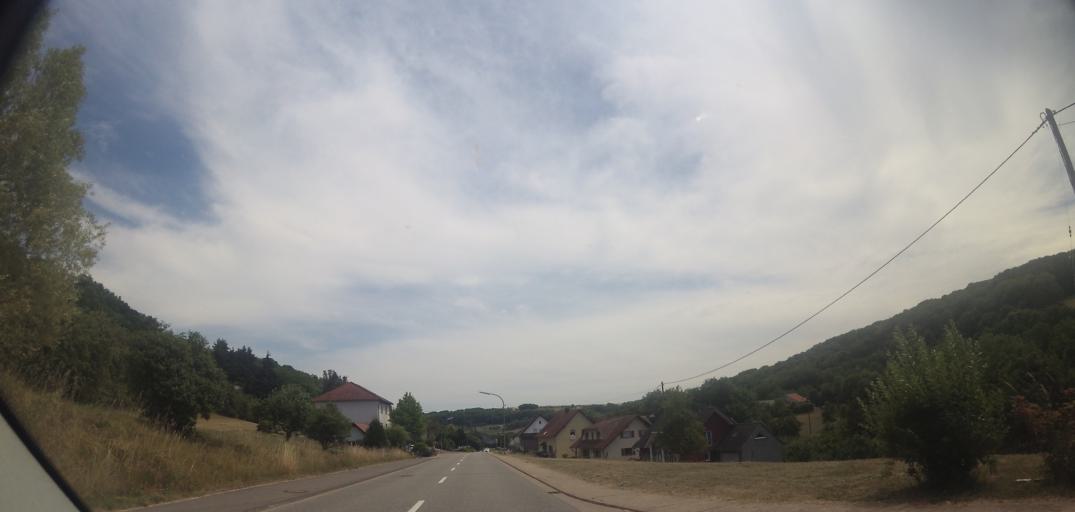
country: DE
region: Saarland
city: Merzig
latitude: 49.4190
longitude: 6.5864
